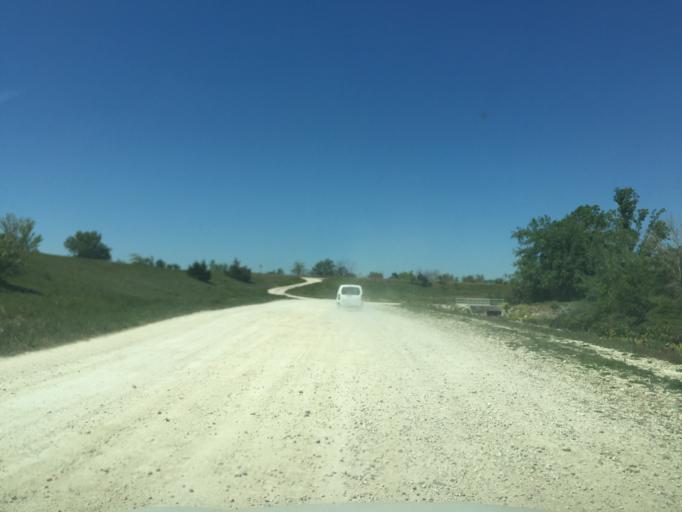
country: FR
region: Languedoc-Roussillon
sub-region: Departement du Gard
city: Roquemaure
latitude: 44.0551
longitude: 4.7915
